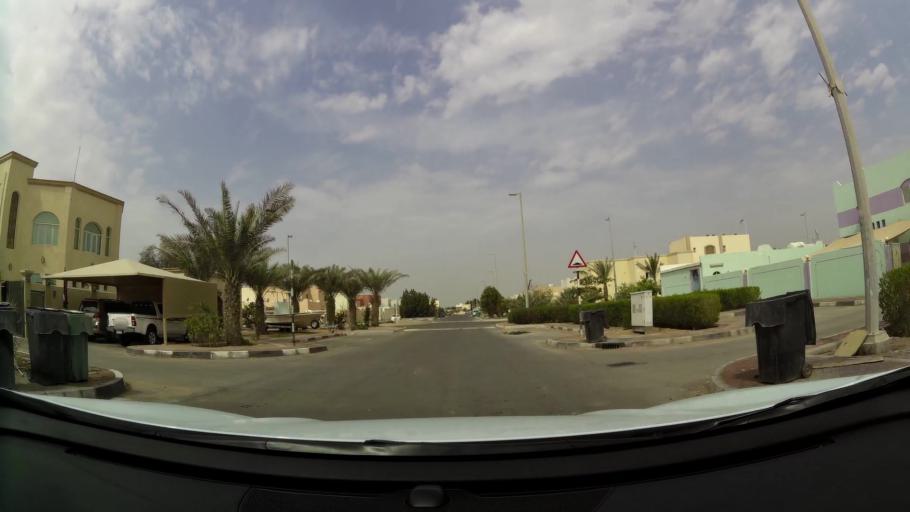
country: AE
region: Abu Dhabi
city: Abu Dhabi
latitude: 24.3110
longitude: 54.6383
